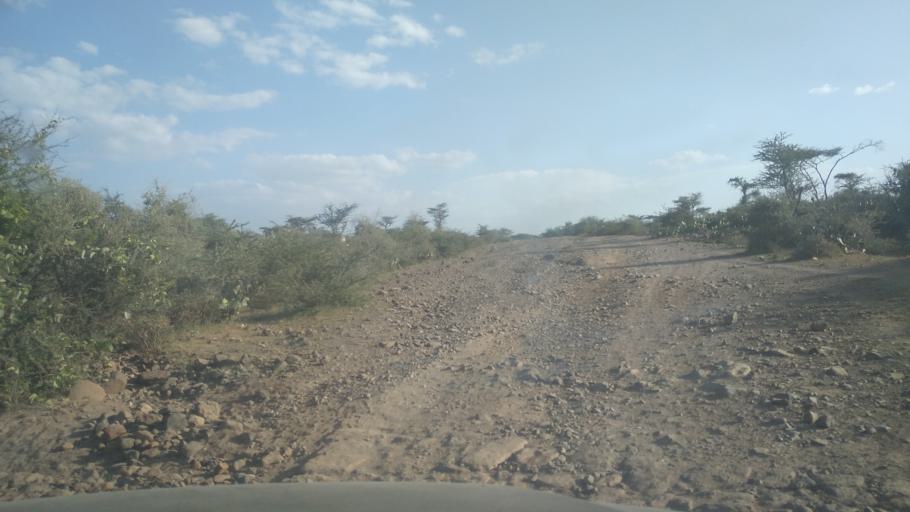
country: ET
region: Oromiya
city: Hirna
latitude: 9.4110
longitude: 40.9560
